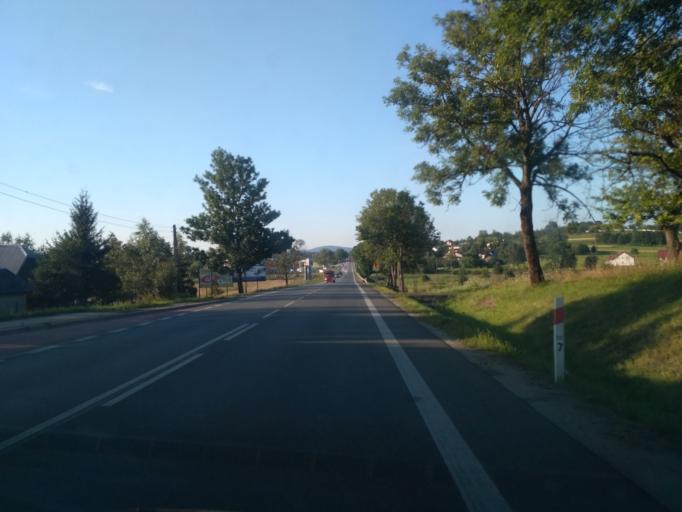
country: PL
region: Subcarpathian Voivodeship
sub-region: Powiat krosnienski
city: Miejsce Piastowe
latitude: 49.6490
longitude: 21.7827
